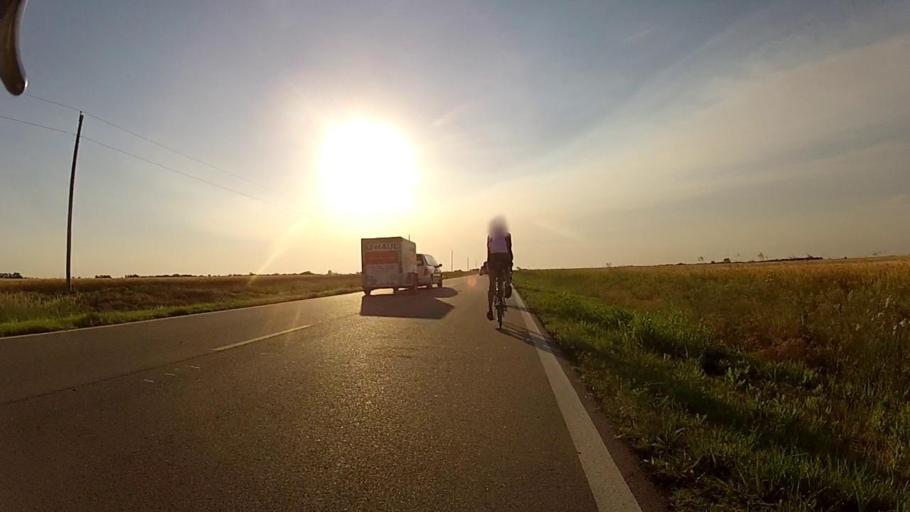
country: US
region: Kansas
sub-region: Harper County
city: Anthony
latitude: 37.1542
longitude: -97.8342
